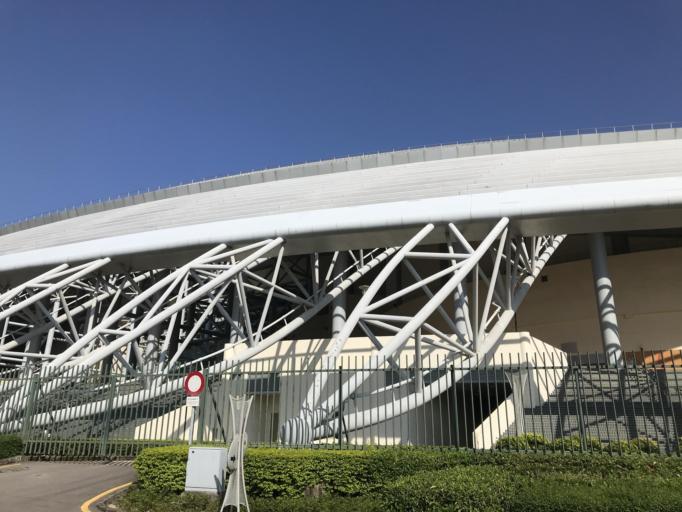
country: MO
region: Macau
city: Macau
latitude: 22.1404
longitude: 113.5691
